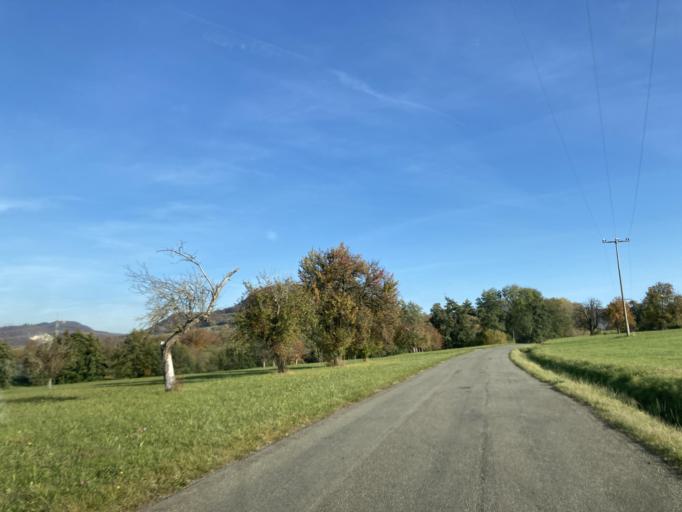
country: DE
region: Baden-Wuerttemberg
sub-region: Tuebingen Region
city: Mossingen
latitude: 48.4022
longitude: 9.0770
